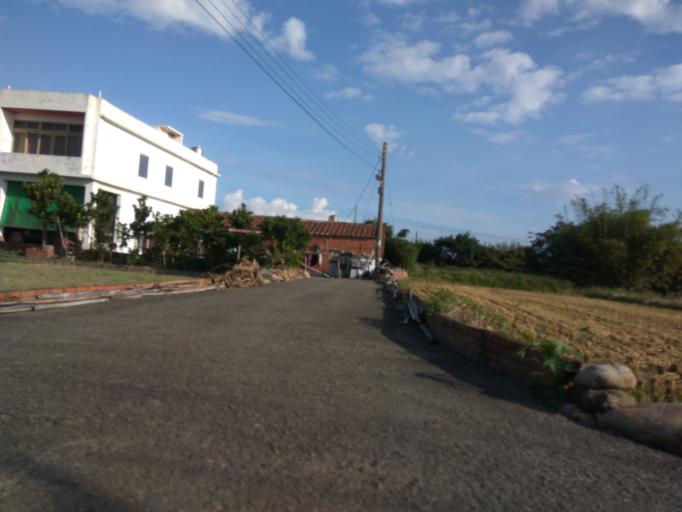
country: TW
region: Taiwan
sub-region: Hsinchu
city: Zhubei
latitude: 24.9778
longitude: 121.0617
